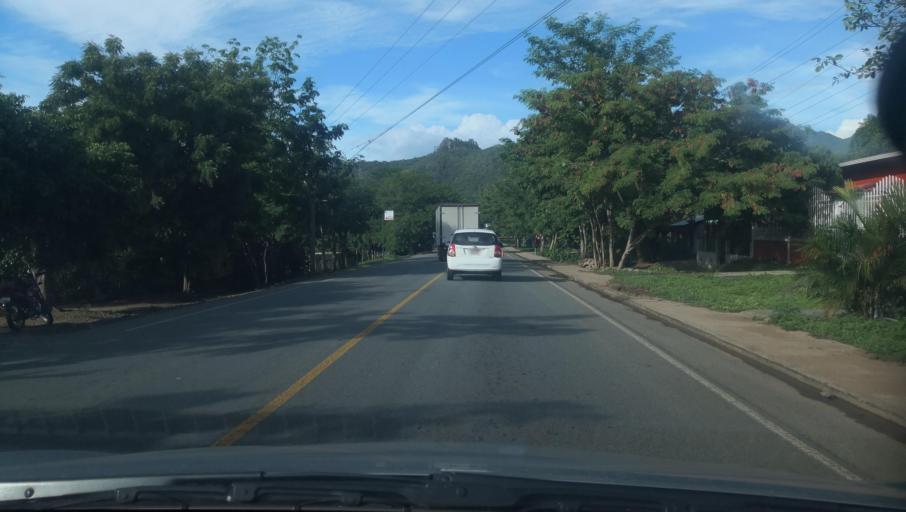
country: NI
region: Madriz
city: Totogalpa
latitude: 13.5609
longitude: -86.4913
